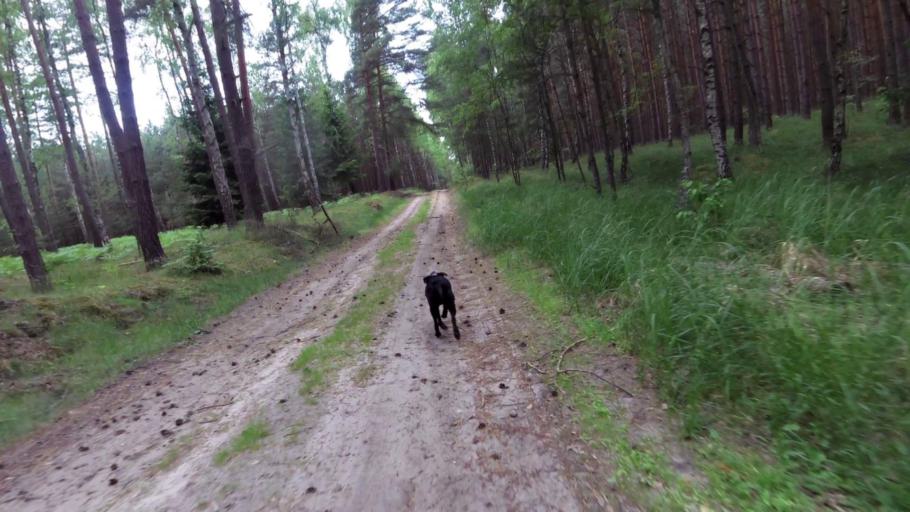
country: PL
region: West Pomeranian Voivodeship
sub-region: Powiat mysliborski
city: Debno
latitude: 52.8155
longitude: 14.6586
